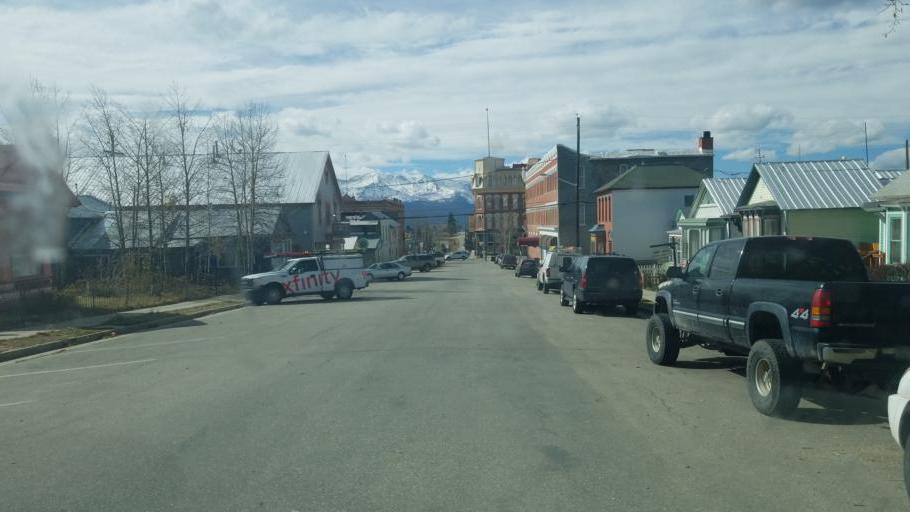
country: US
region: Colorado
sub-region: Lake County
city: Leadville
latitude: 39.2499
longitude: -106.2907
